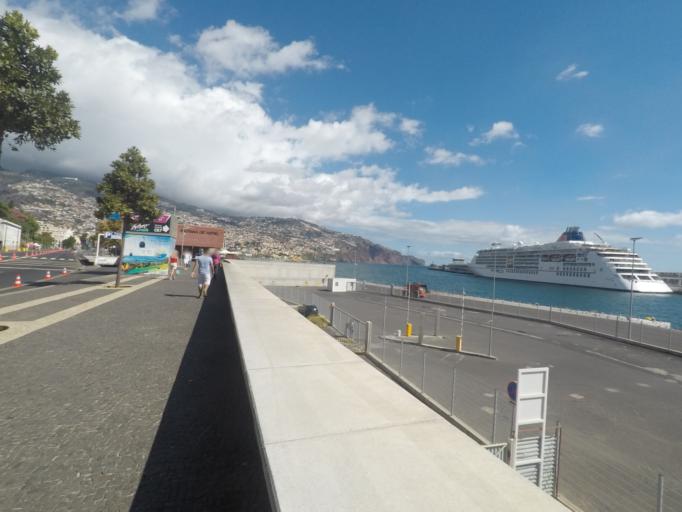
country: PT
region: Madeira
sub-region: Funchal
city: Funchal
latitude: 32.6430
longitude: -16.9158
